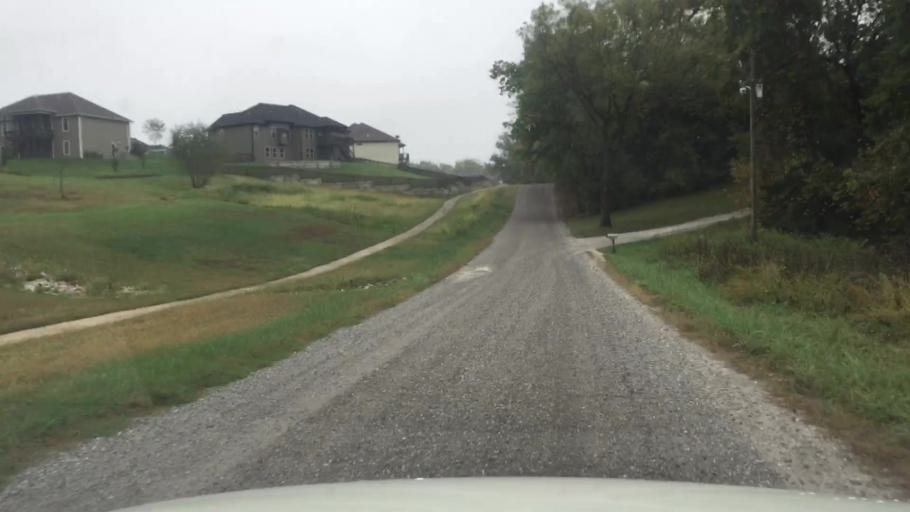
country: US
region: Missouri
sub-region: Boone County
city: Columbia
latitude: 38.8903
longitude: -92.4196
